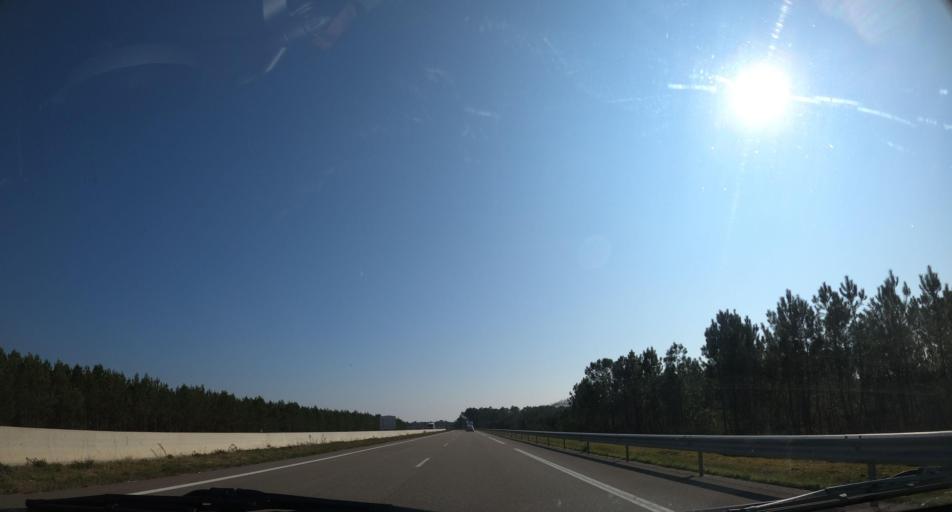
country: FR
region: Aquitaine
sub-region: Departement des Landes
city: Saint-Geours-de-Maremne
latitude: 43.6952
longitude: -1.2162
